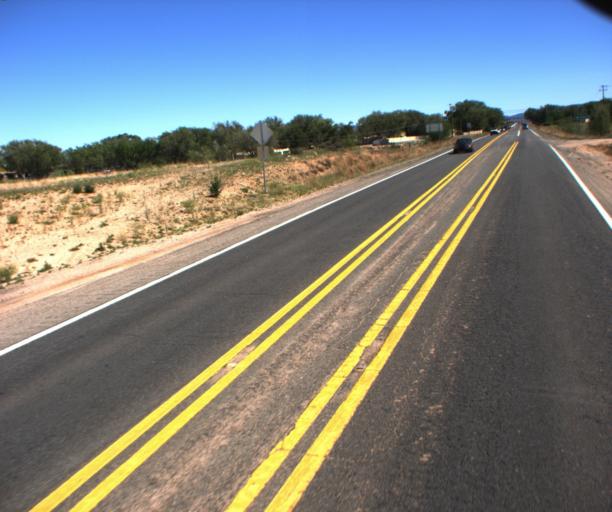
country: US
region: Arizona
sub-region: Yavapai County
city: Chino Valley
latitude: 34.6497
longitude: -112.4342
